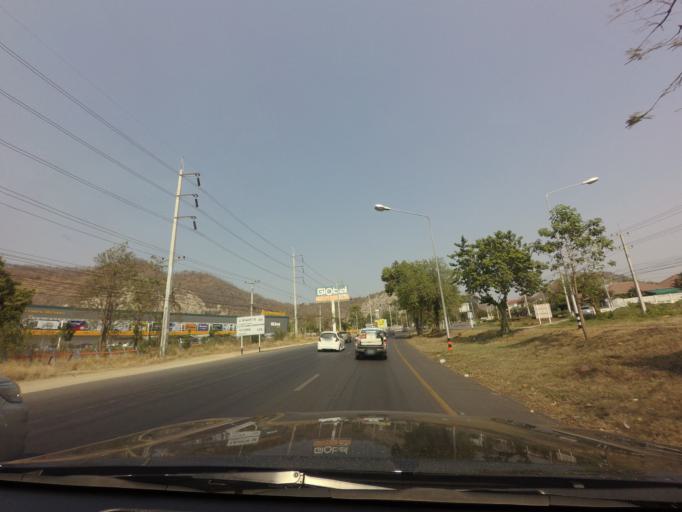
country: TH
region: Kanchanaburi
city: Kanchanaburi
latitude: 14.0653
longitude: 99.4950
